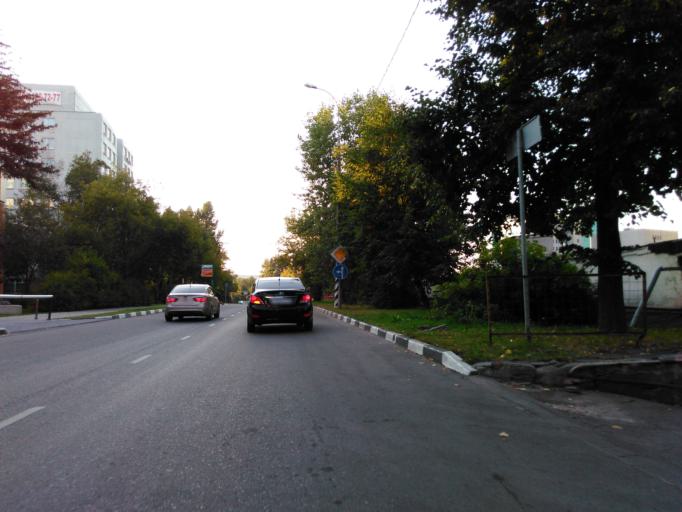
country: RU
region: Moskovskaya
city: Cheremushki
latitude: 55.6560
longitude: 37.5560
